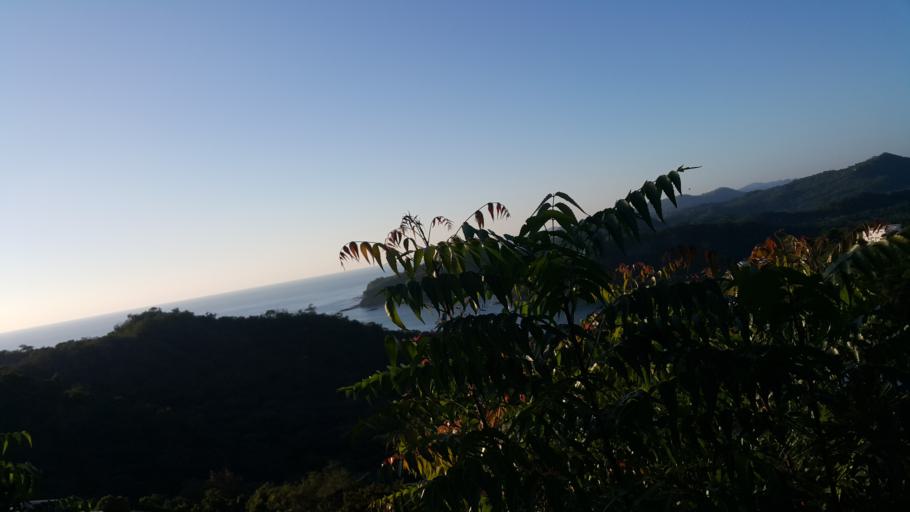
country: NI
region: Rivas
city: San Juan del Sur
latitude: 11.2623
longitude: -85.8820
